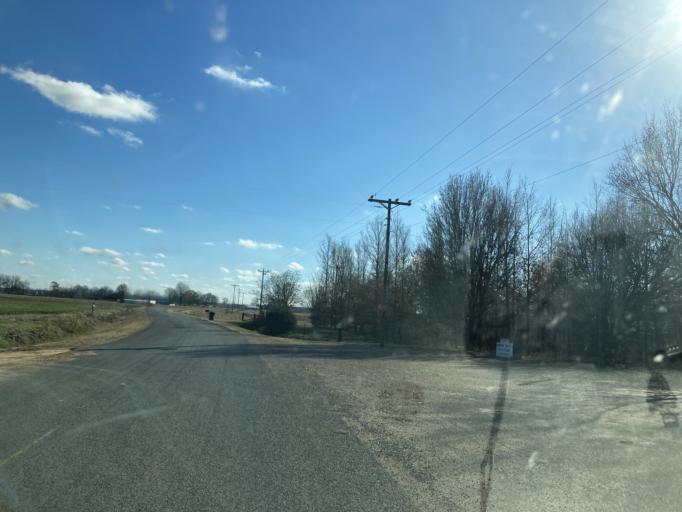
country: US
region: Mississippi
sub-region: Yazoo County
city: Yazoo City
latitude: 32.9318
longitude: -90.4727
